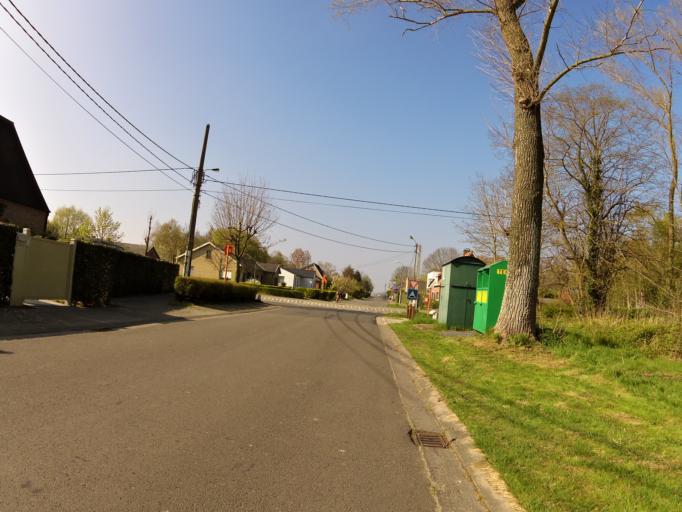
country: BE
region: Flanders
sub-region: Provincie West-Vlaanderen
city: Gistel
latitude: 51.1256
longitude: 2.9684
